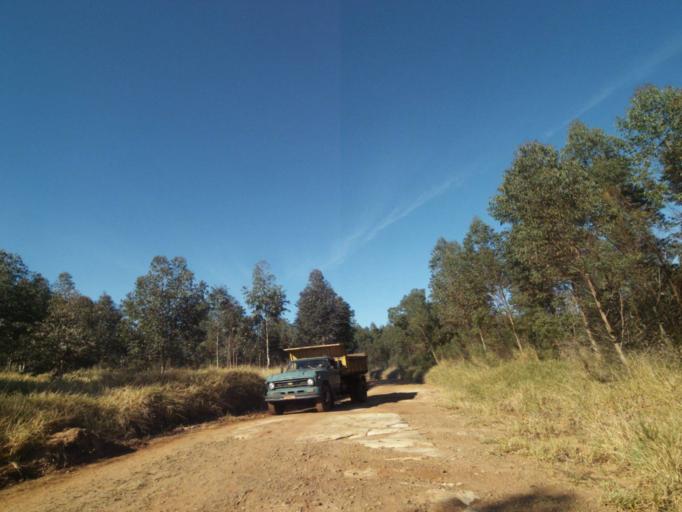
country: BR
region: Parana
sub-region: Tibagi
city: Tibagi
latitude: -24.5377
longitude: -50.3689
